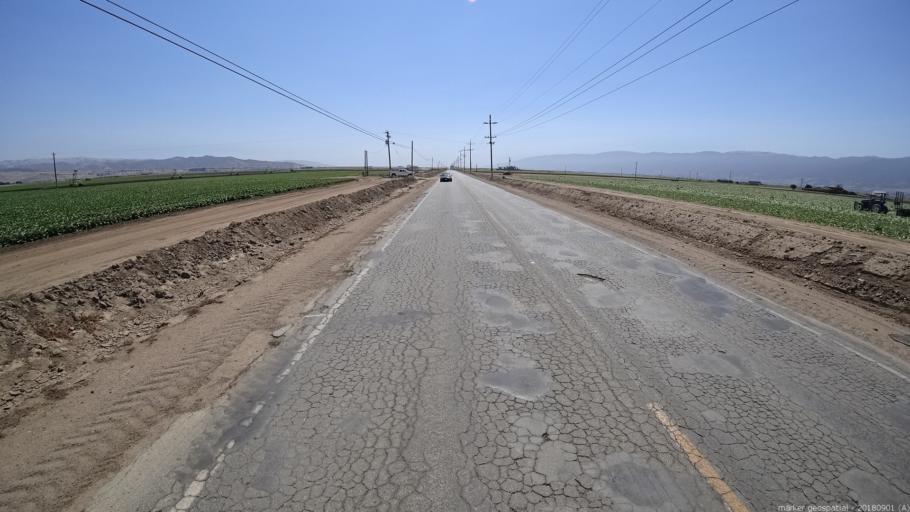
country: US
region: California
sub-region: Monterey County
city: Chualar
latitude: 36.6124
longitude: -121.5194
